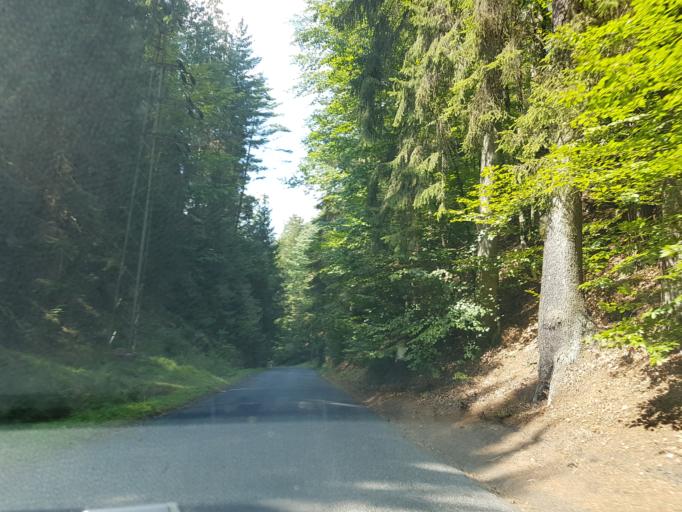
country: CZ
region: Ustecky
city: Ceska Kamenice
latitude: 50.8512
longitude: 14.4068
